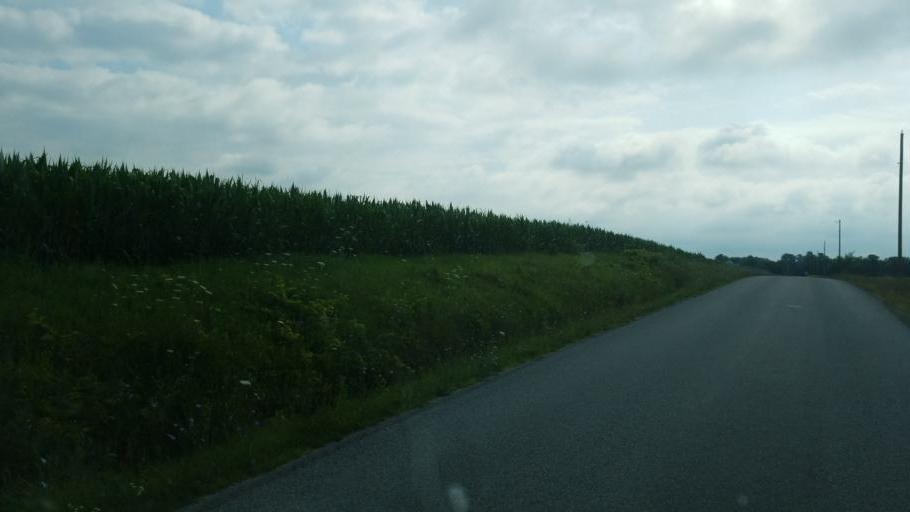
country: US
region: Ohio
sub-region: Knox County
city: Centerburg
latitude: 40.3196
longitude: -82.6835
